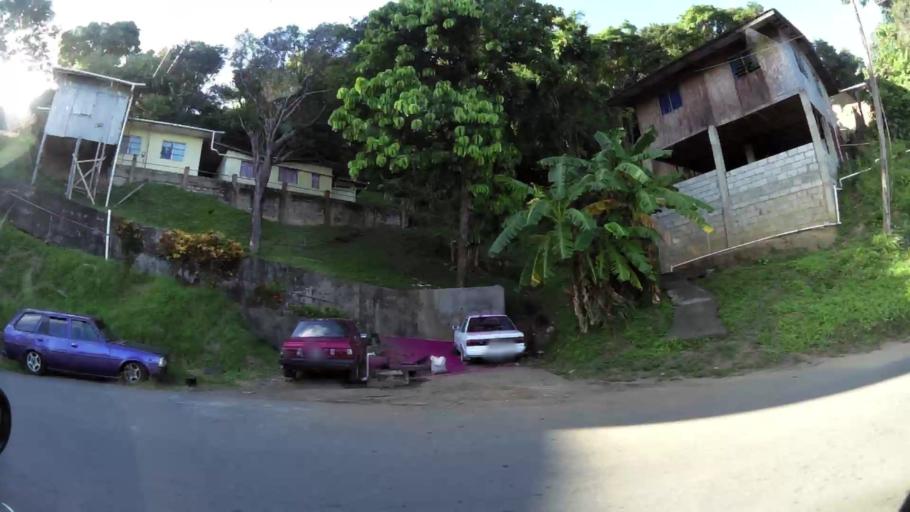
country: TT
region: Eastern Tobago
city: Roxborough
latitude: 11.2318
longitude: -60.5989
